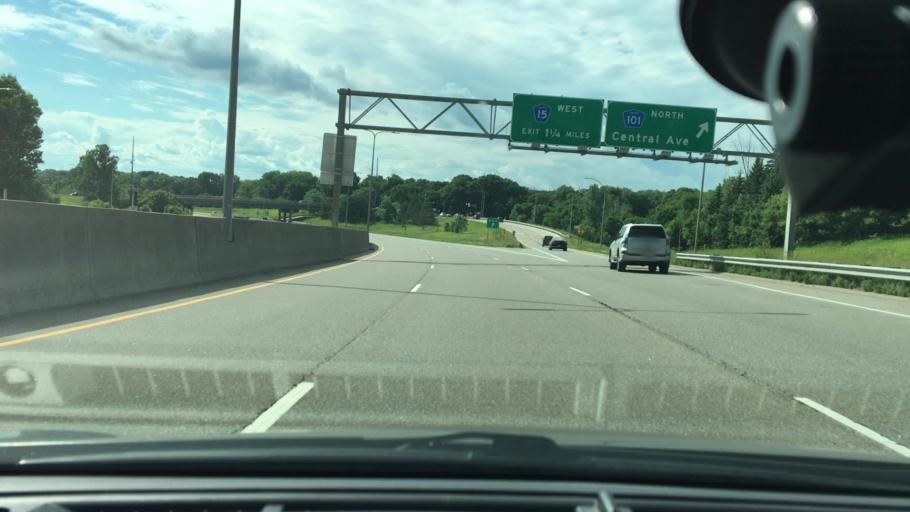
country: US
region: Minnesota
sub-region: Hennepin County
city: Wayzata
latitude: 44.9749
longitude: -93.4980
